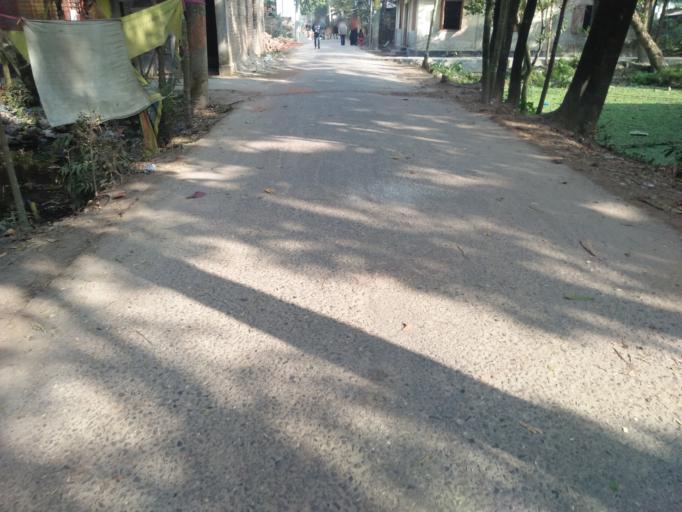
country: BD
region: Barisal
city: Bhola
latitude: 22.6792
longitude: 90.6424
